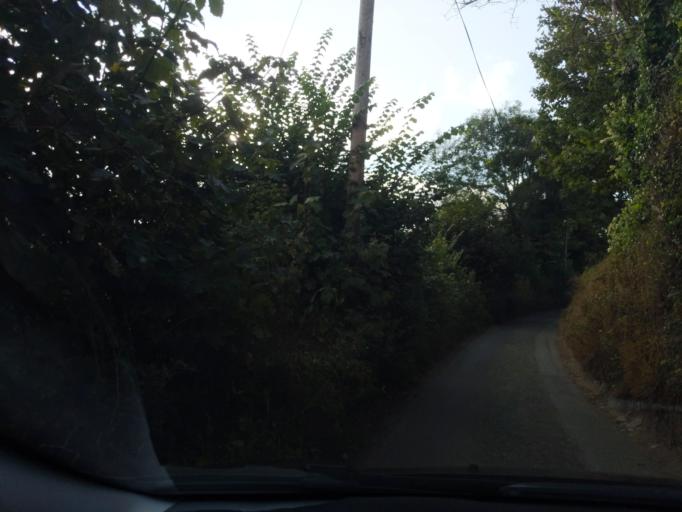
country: GB
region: England
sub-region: Devon
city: Salcombe
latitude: 50.2302
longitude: -3.7964
